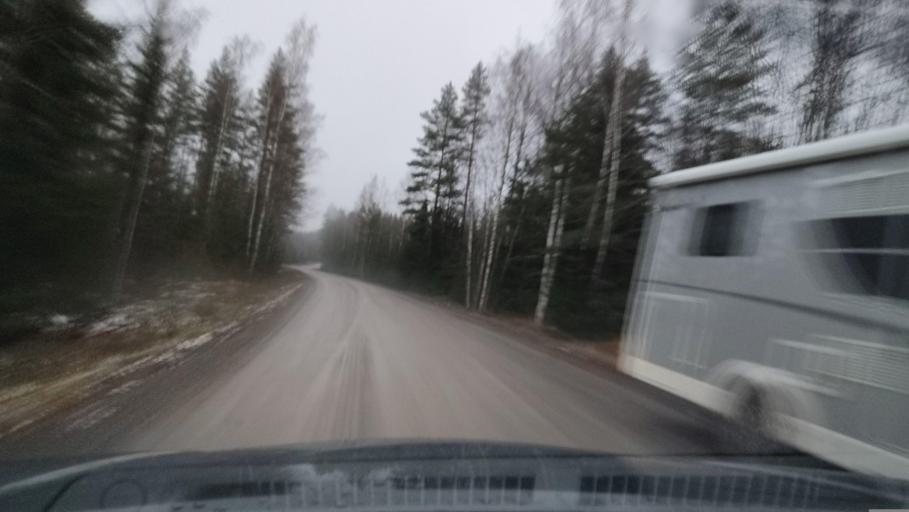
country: FI
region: Southern Ostrobothnia
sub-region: Suupohja
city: Karijoki
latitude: 62.1269
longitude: 21.6096
